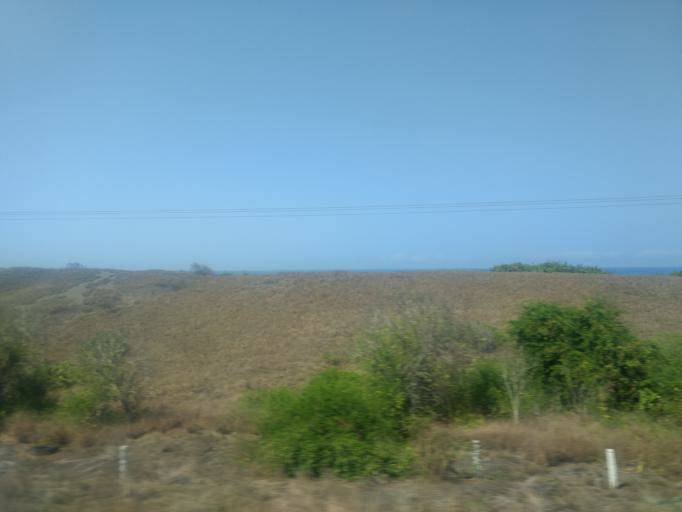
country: MX
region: Colima
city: Armeria
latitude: 18.9463
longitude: -104.1172
